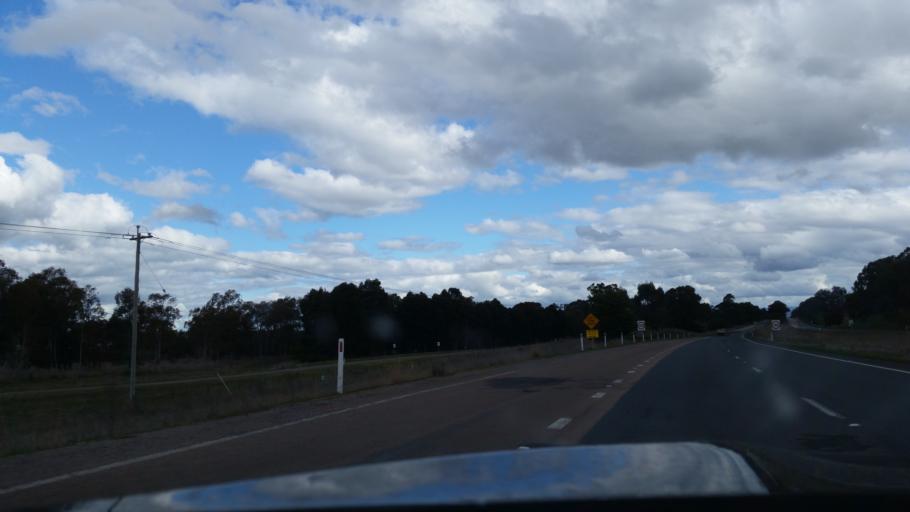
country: AU
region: New South Wales
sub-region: Albury Municipality
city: Lavington
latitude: -35.9727
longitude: 147.0040
